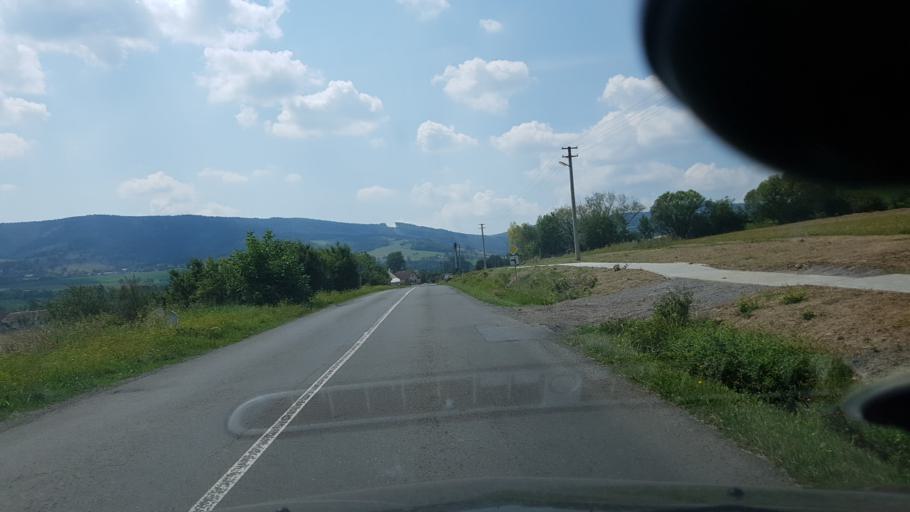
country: SK
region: Banskobystricky
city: Detva
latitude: 48.5135
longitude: 19.3081
